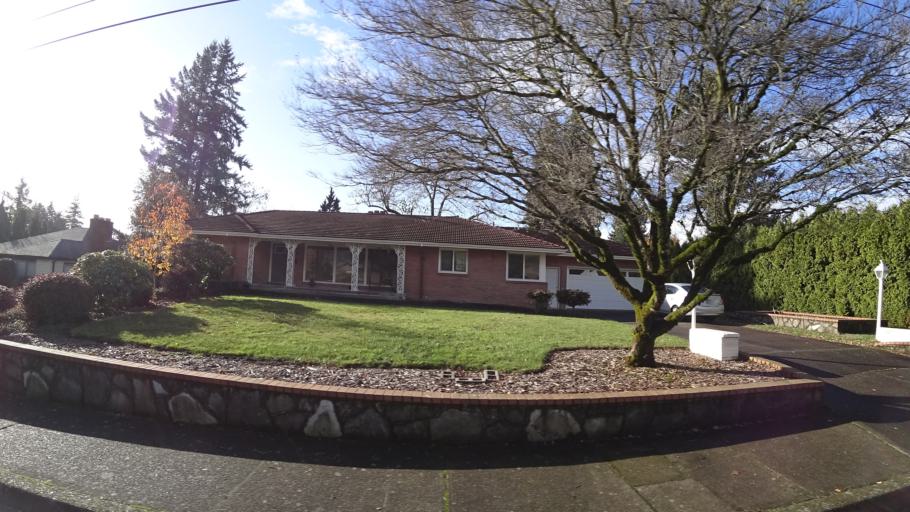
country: US
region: Oregon
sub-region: Multnomah County
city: Lents
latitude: 45.5272
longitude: -122.5447
